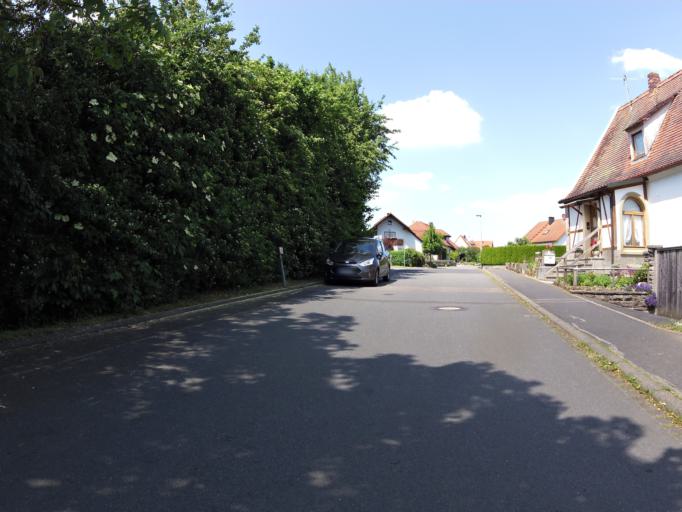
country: DE
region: Bavaria
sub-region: Regierungsbezirk Unterfranken
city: Kleinrinderfeld
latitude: 49.7014
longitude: 9.8391
